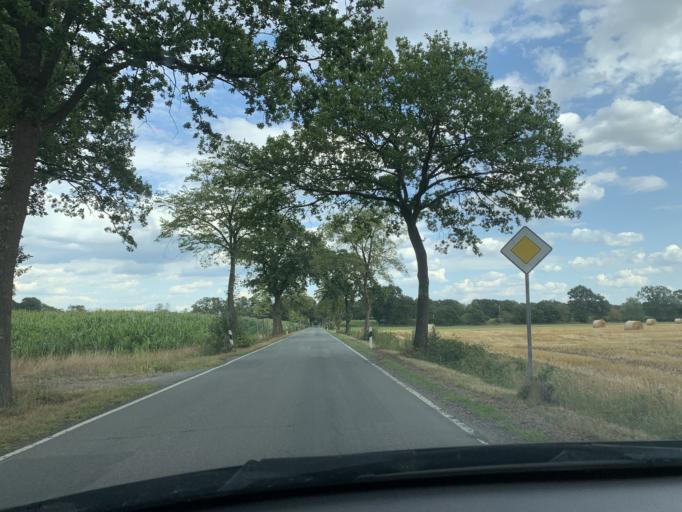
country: DE
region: Lower Saxony
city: Apen
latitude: 53.2208
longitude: 7.8634
